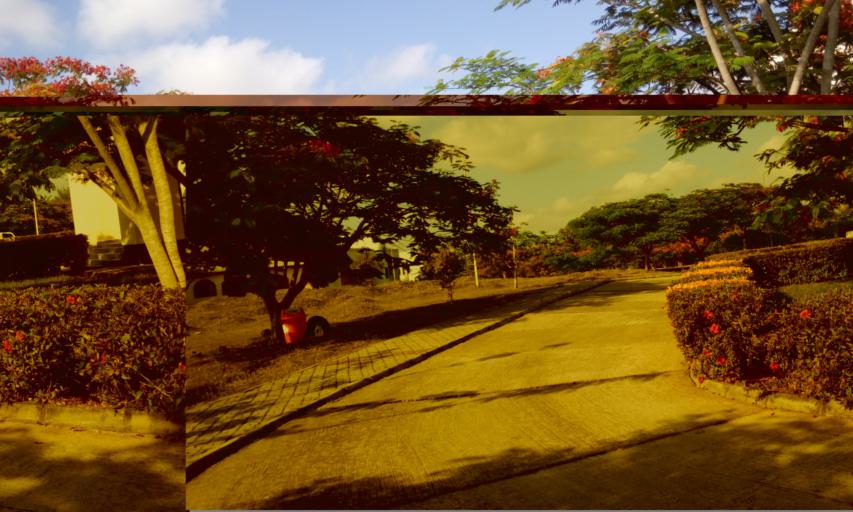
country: TZ
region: Zanzibar Central/South
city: Koani
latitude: -6.2003
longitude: 39.3059
